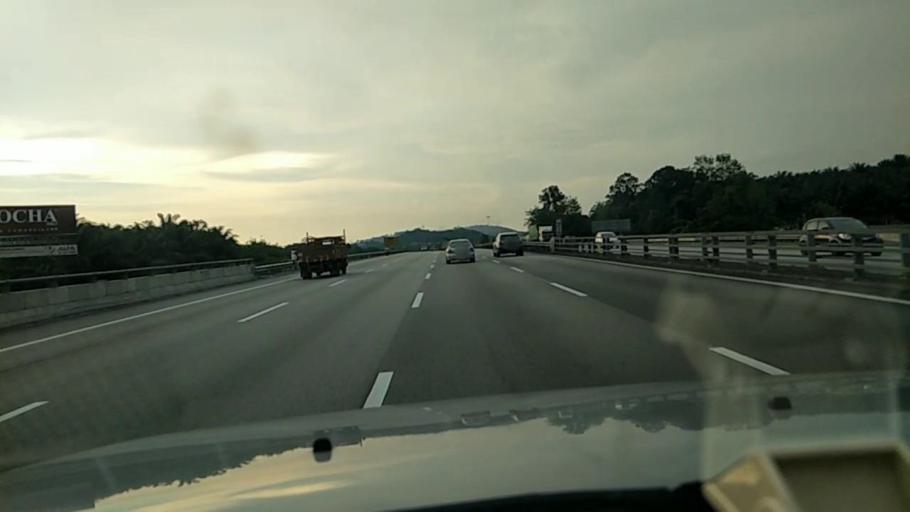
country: MY
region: Selangor
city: Kuang
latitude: 3.2615
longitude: 101.5539
